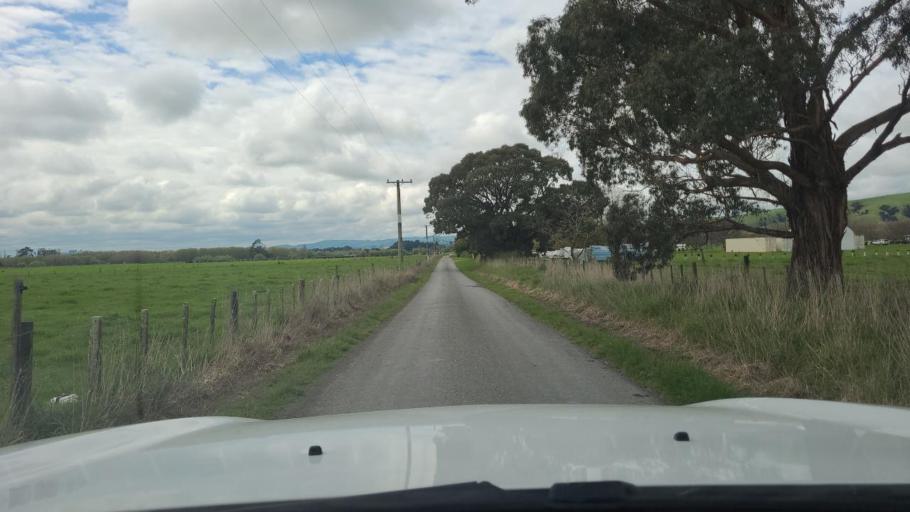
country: NZ
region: Wellington
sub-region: Masterton District
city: Masterton
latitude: -41.0957
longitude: 175.4914
